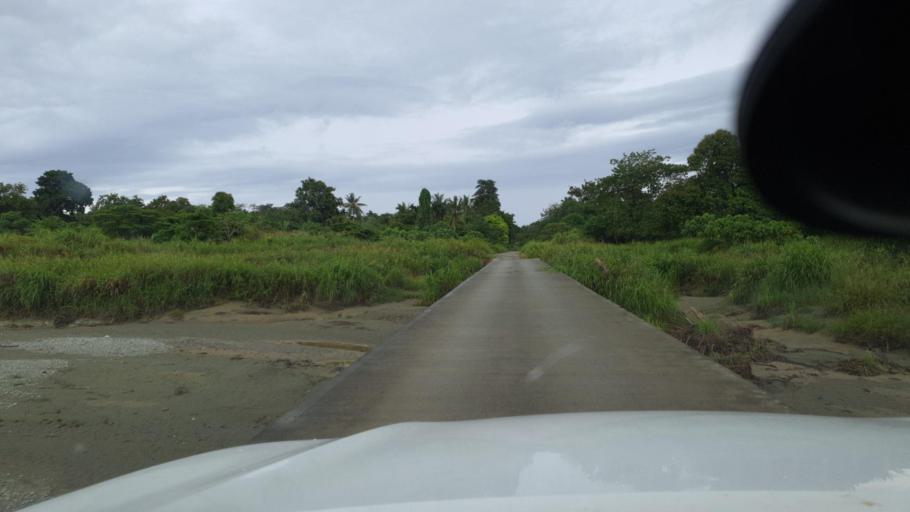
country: SB
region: Guadalcanal
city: Honiara
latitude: -9.4653
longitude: 160.3600
